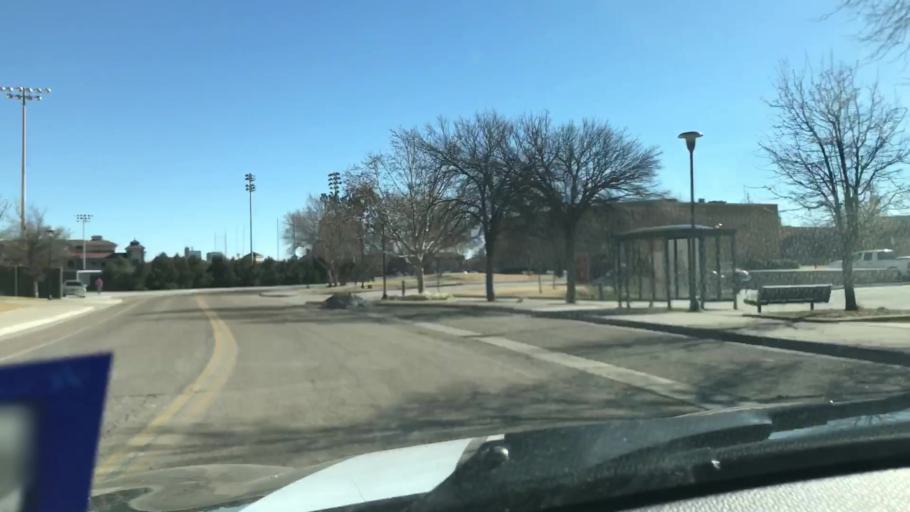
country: US
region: Texas
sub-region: Lubbock County
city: Lubbock
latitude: 33.5888
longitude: -101.8739
